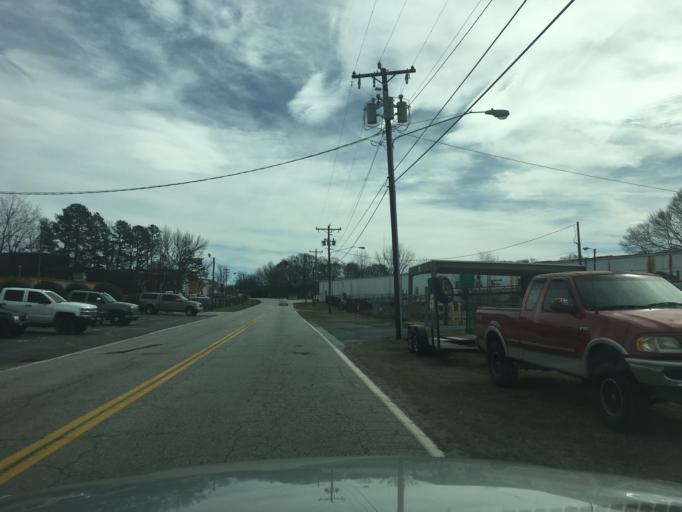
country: US
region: South Carolina
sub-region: Greenville County
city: Greenville
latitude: 34.8464
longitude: -82.3594
